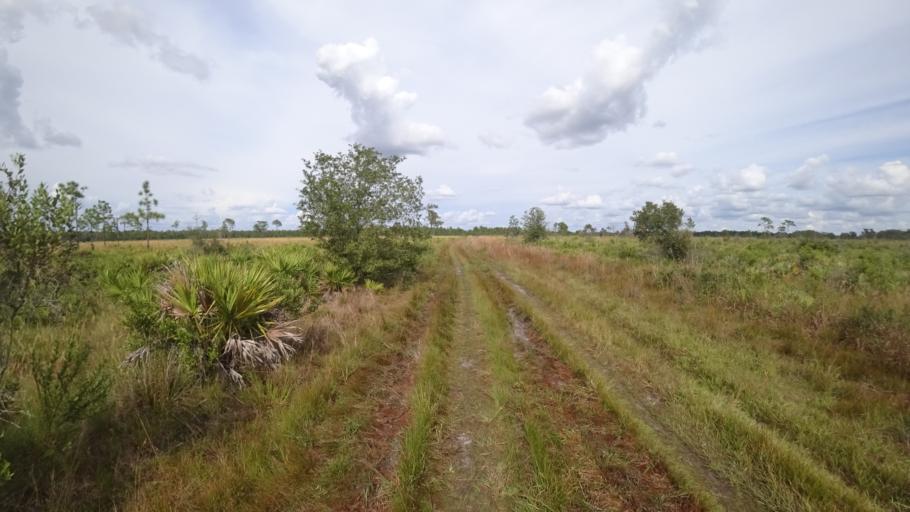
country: US
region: Florida
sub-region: Hillsborough County
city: Wimauma
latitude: 27.5611
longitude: -82.1424
